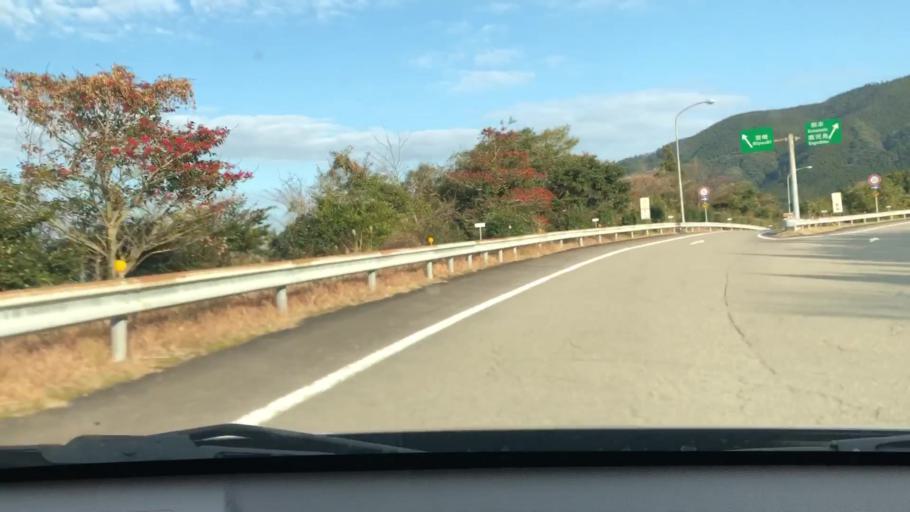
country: JP
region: Miyazaki
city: Miyazaki-shi
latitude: 31.8222
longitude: 131.3013
